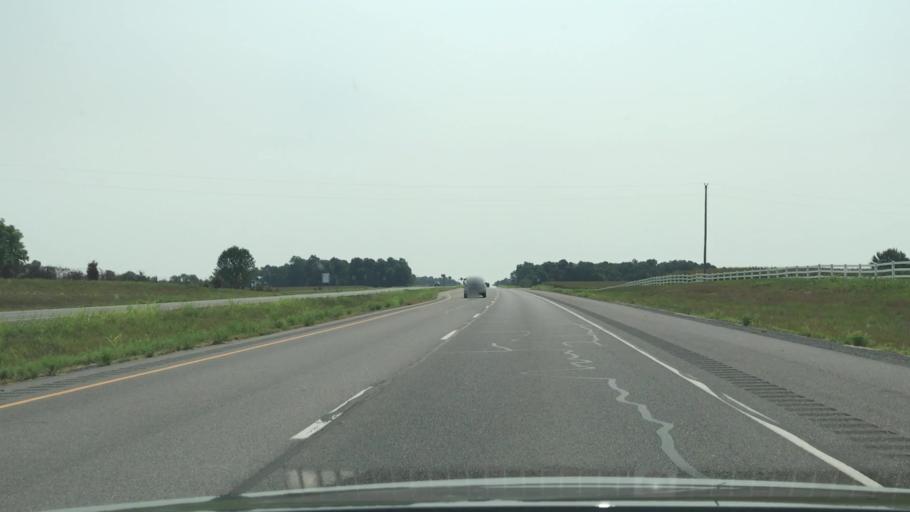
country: US
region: Kentucky
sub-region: Graves County
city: Mayfield
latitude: 36.6785
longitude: -88.5265
